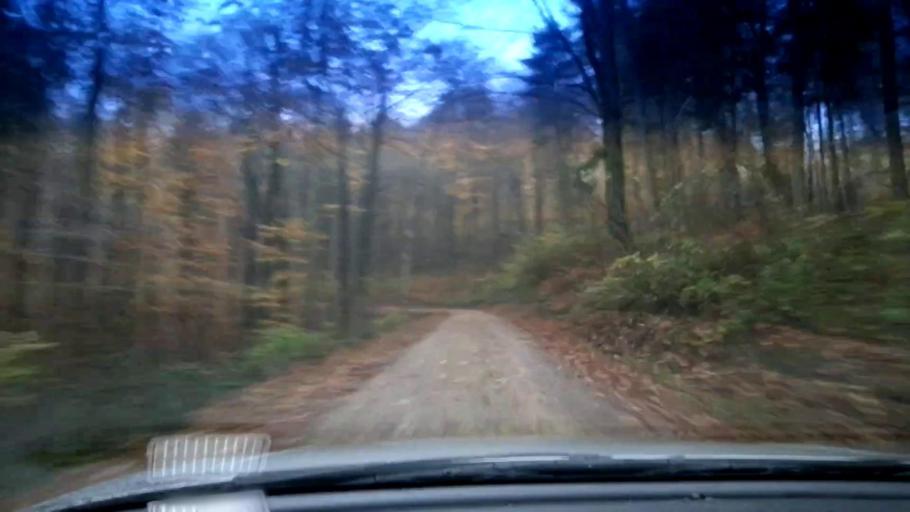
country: DE
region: Bavaria
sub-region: Upper Franconia
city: Litzendorf
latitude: 49.9400
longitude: 11.0293
